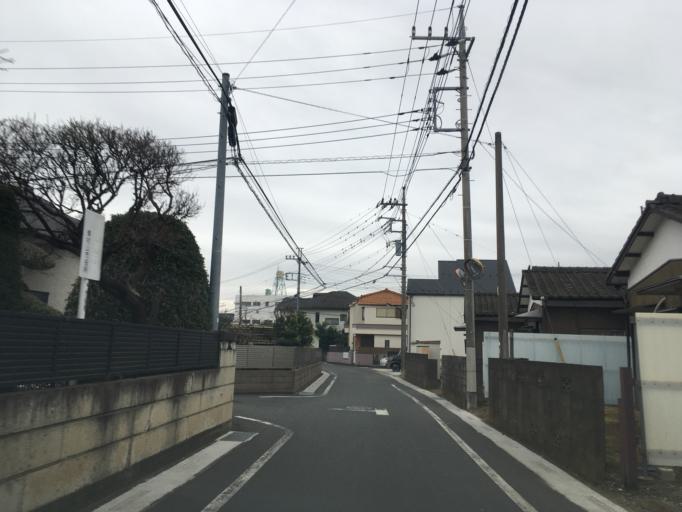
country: JP
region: Tokyo
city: Higashimurayama-shi
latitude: 35.7517
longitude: 139.4841
